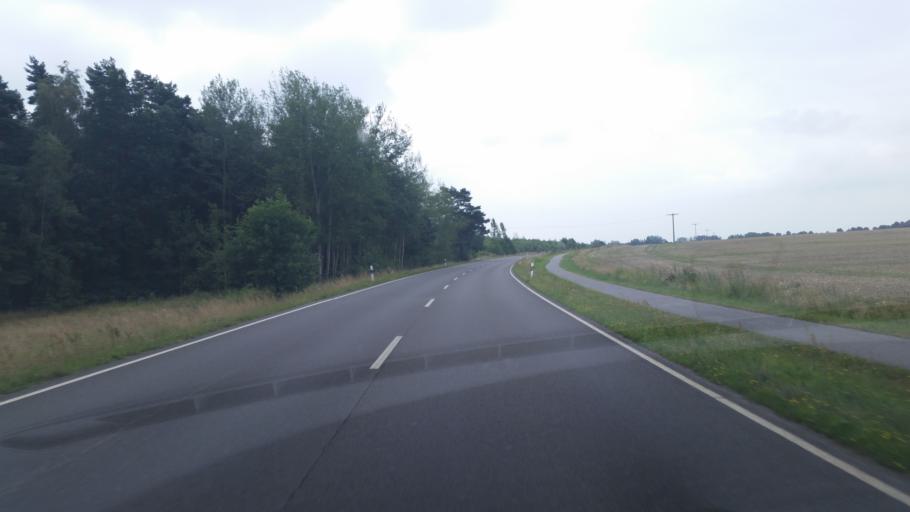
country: DE
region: Brandenburg
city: Senftenberg
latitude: 51.4795
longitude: 14.0701
